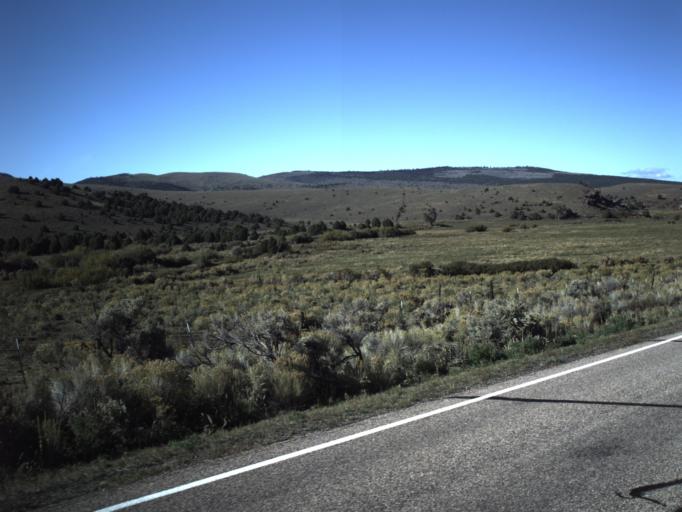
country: US
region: Utah
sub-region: Garfield County
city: Panguitch
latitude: 37.7567
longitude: -112.5617
